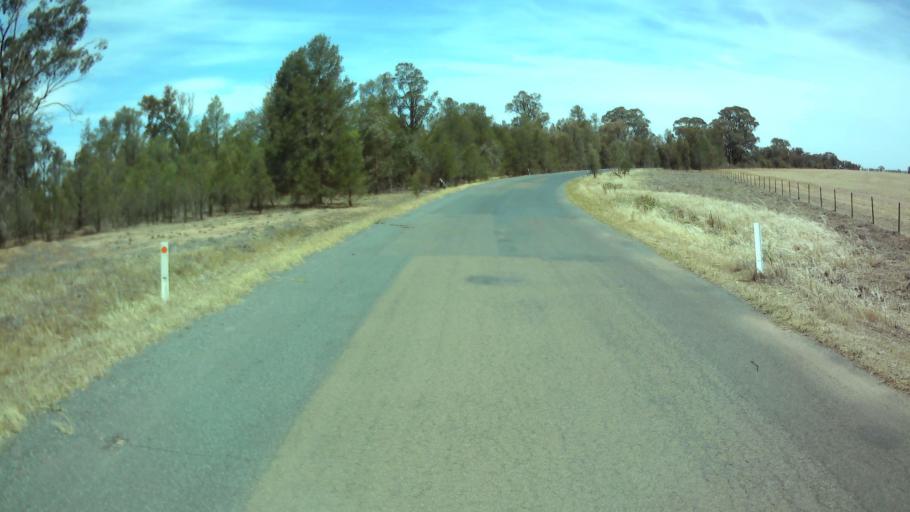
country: AU
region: New South Wales
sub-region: Weddin
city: Grenfell
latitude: -33.9446
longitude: 147.7787
